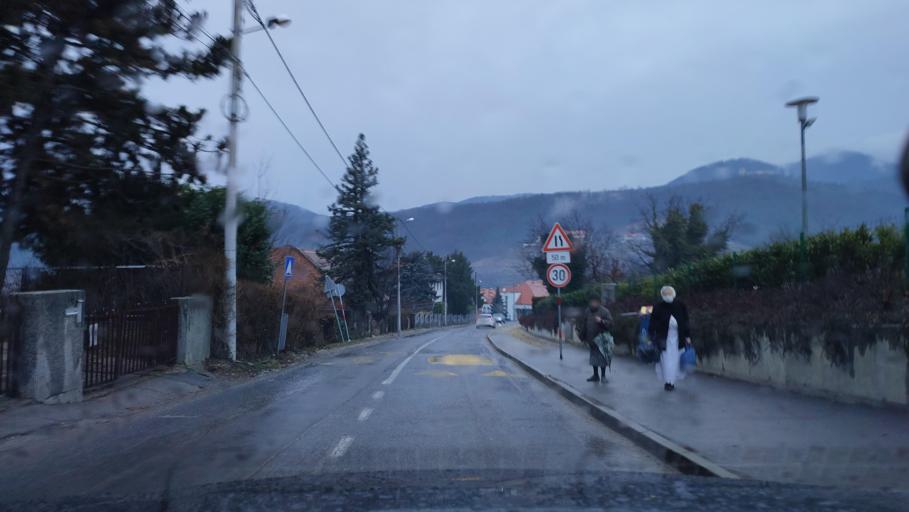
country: HR
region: Grad Zagreb
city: Zagreb
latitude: 45.8511
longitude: 15.9513
